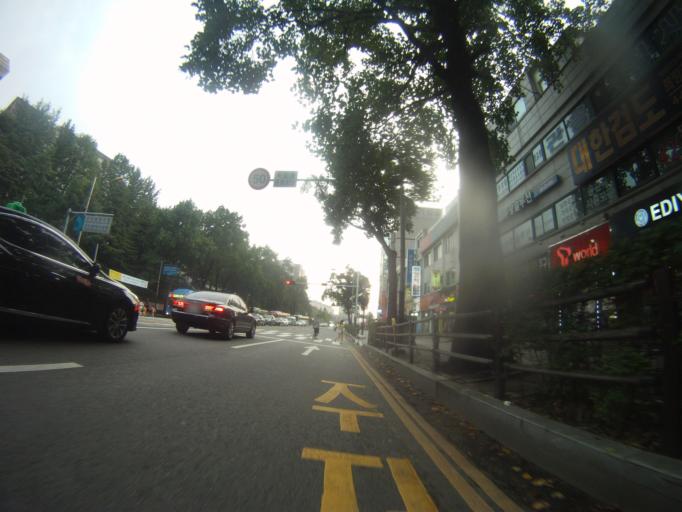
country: KR
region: Incheon
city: Incheon
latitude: 37.4575
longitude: 126.6931
